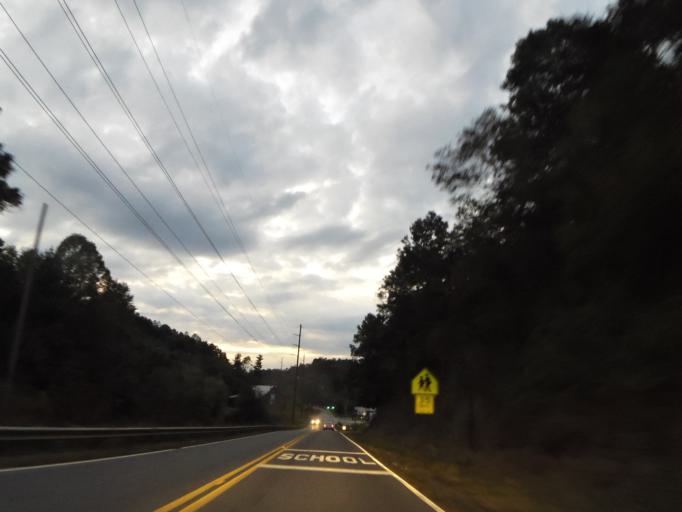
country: US
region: North Carolina
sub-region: Madison County
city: Marshall
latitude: 35.8371
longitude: -82.7143
